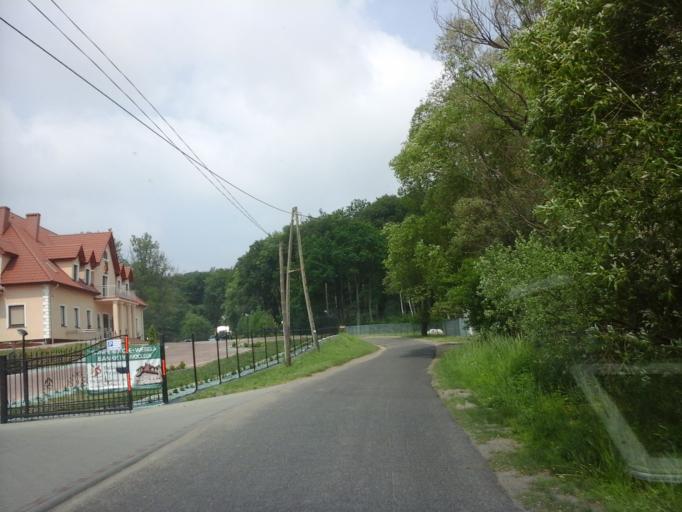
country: PL
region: West Pomeranian Voivodeship
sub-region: Powiat mysliborski
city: Barlinek
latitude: 53.0100
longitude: 15.2247
